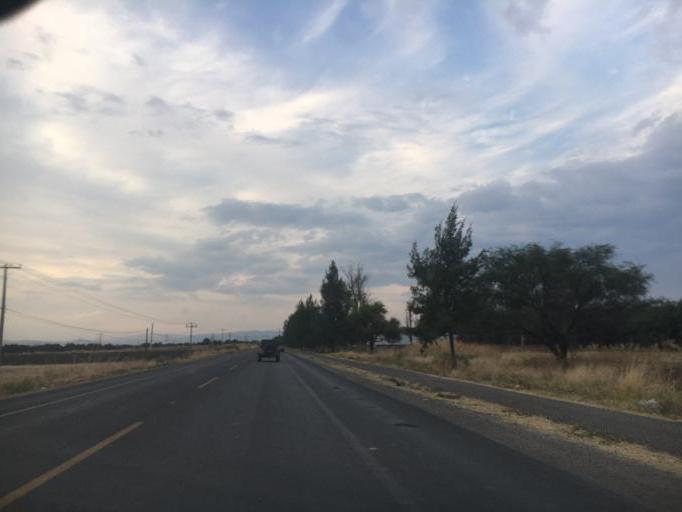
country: MX
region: Guanajuato
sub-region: Leon
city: El CERESO
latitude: 21.0042
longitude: -101.7021
